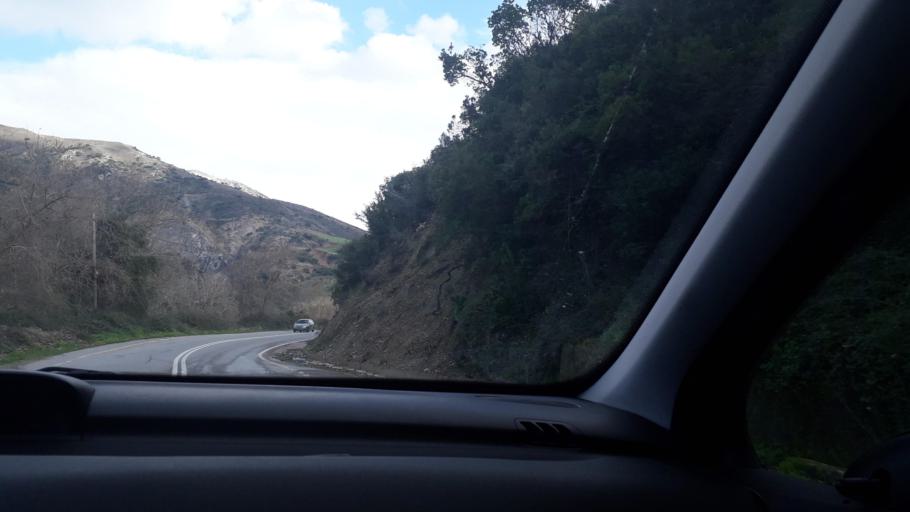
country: GR
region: Crete
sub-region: Nomos Rethymnis
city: Agia Foteini
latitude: 35.2935
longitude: 24.5567
